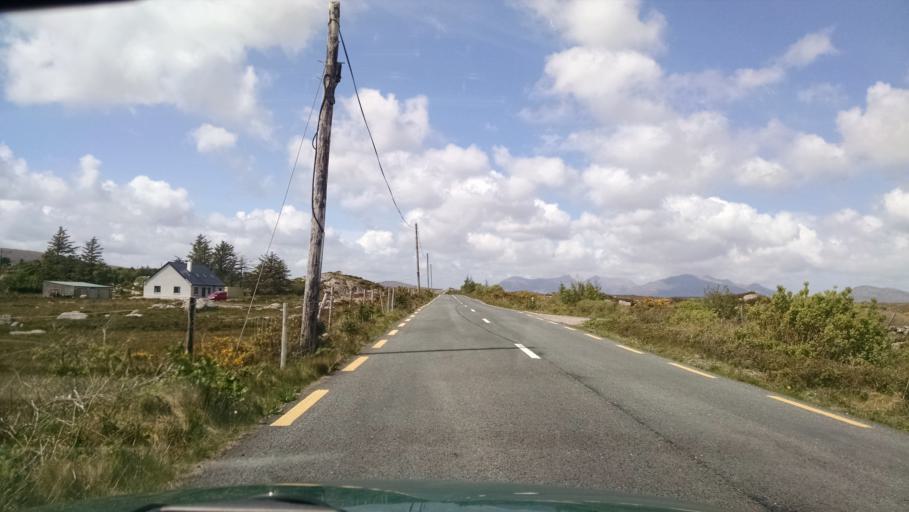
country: IE
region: Connaught
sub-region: County Galway
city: Oughterard
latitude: 53.3900
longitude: -9.6344
